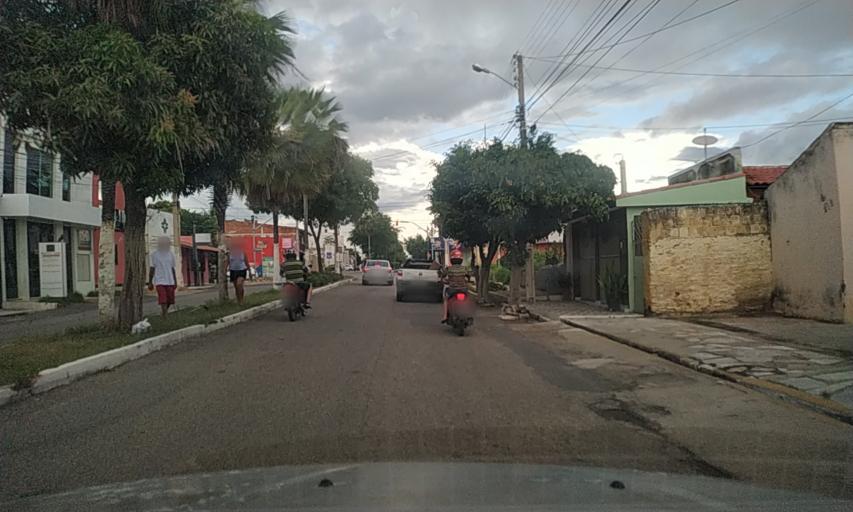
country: BR
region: Rio Grande do Norte
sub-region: Mossoro
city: Mossoro
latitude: -5.1875
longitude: -37.3515
